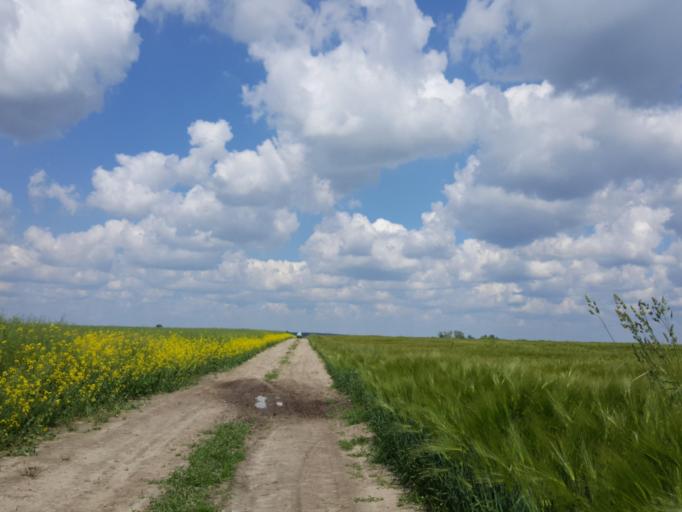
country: BY
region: Brest
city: Kamyanyets
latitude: 52.4088
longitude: 23.7456
